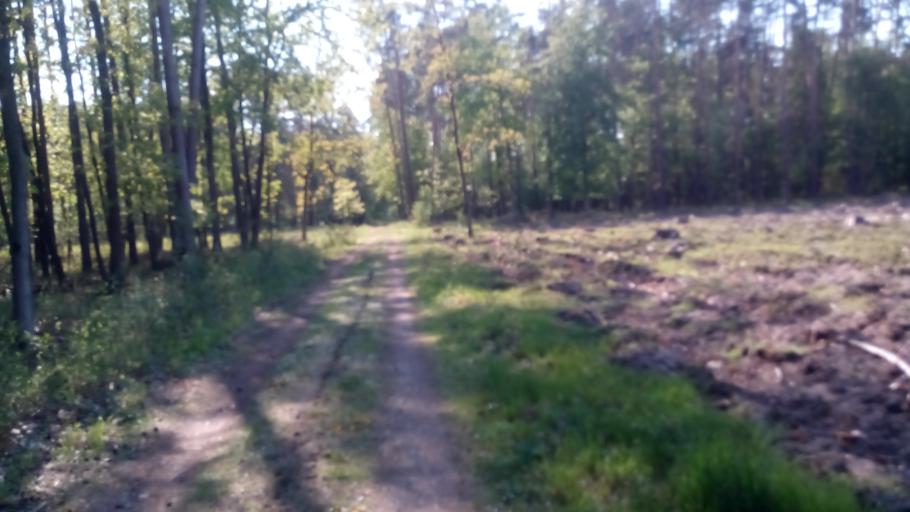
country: PL
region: Opole Voivodeship
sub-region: Powiat opolski
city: Tarnow Opolski
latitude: 50.5846
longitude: 18.0719
